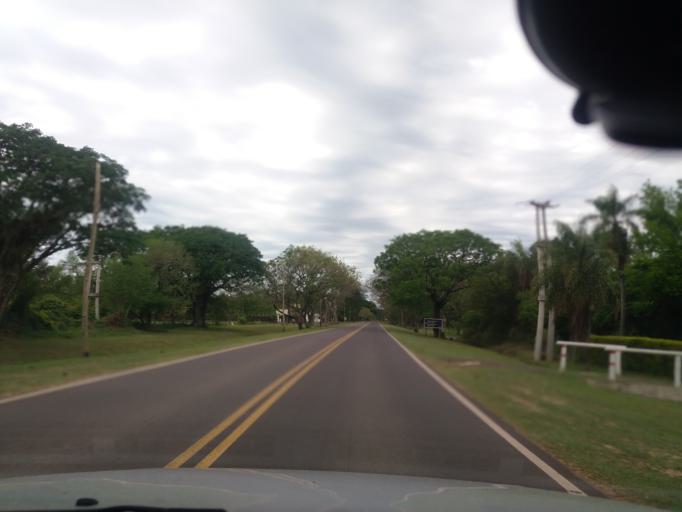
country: AR
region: Corrientes
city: San Luis del Palmar
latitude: -27.4570
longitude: -58.6762
